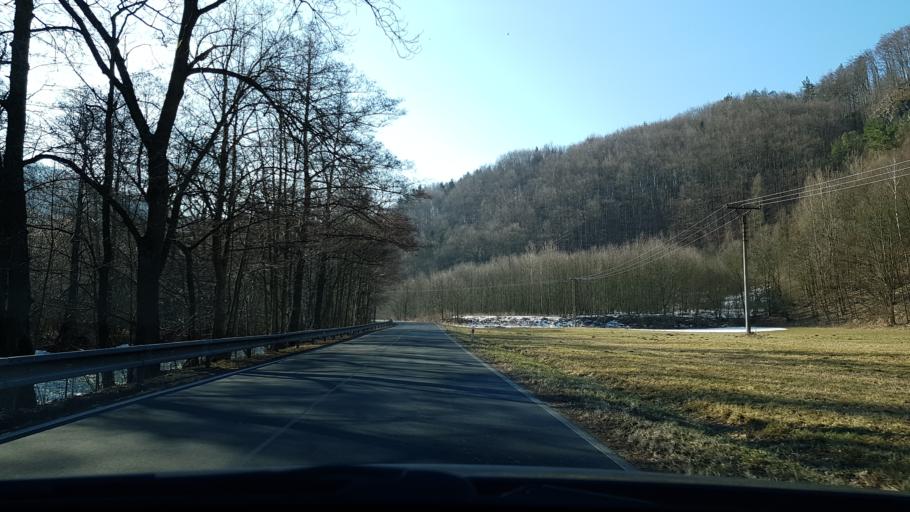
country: CZ
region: Olomoucky
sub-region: Okres Sumperk
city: Hanusovice
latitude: 50.0478
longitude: 16.9151
